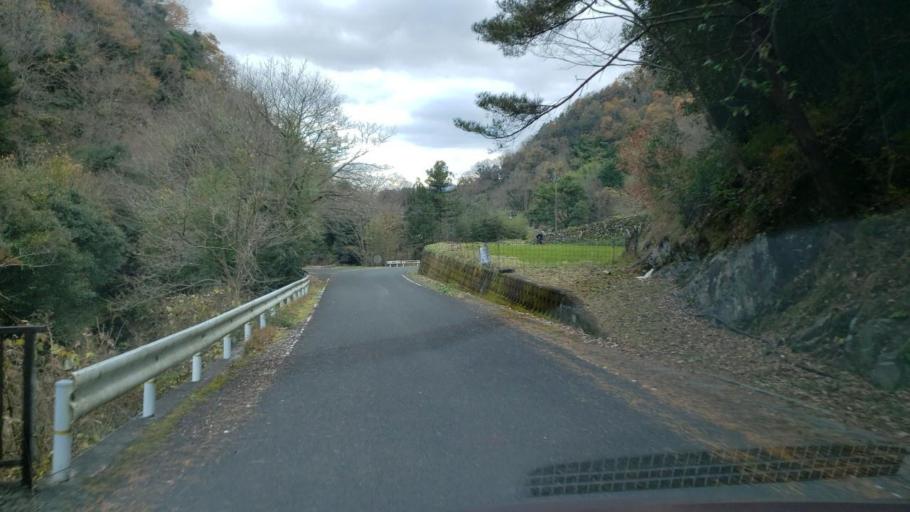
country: JP
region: Tokushima
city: Wakimachi
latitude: 34.1314
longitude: 134.2282
